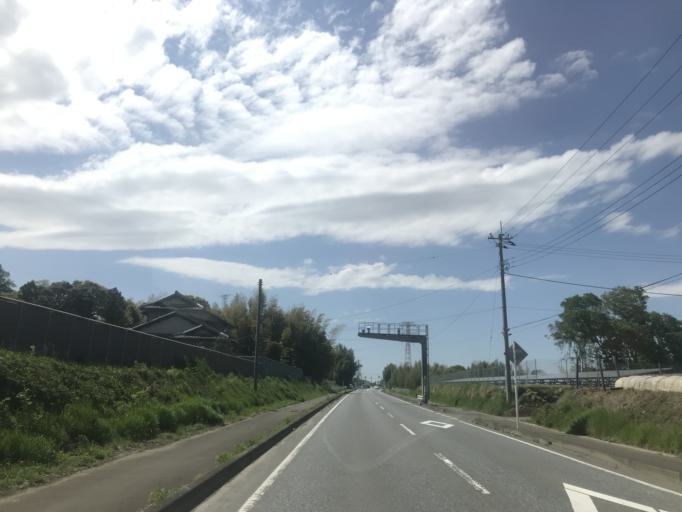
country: JP
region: Chiba
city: Noda
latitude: 35.9666
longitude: 139.8969
